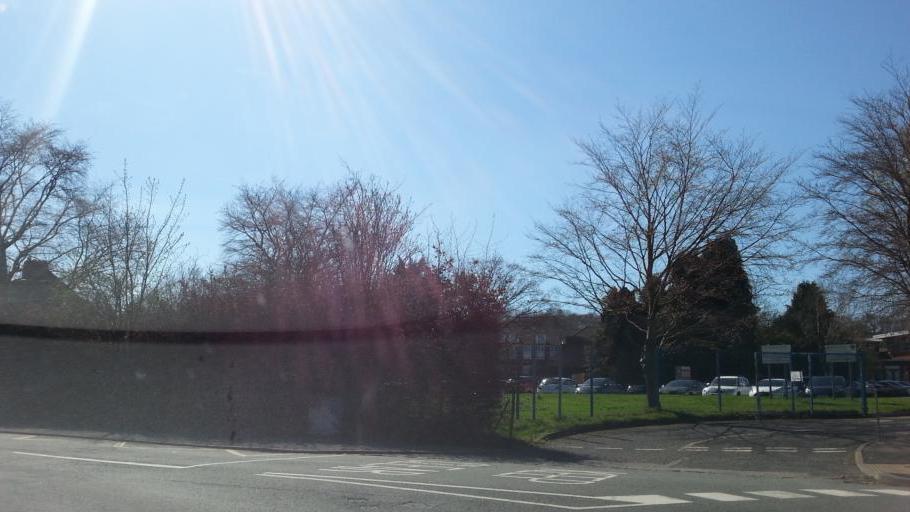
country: GB
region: England
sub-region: Worcestershire
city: Barnt Green
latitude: 52.3916
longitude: -2.0299
